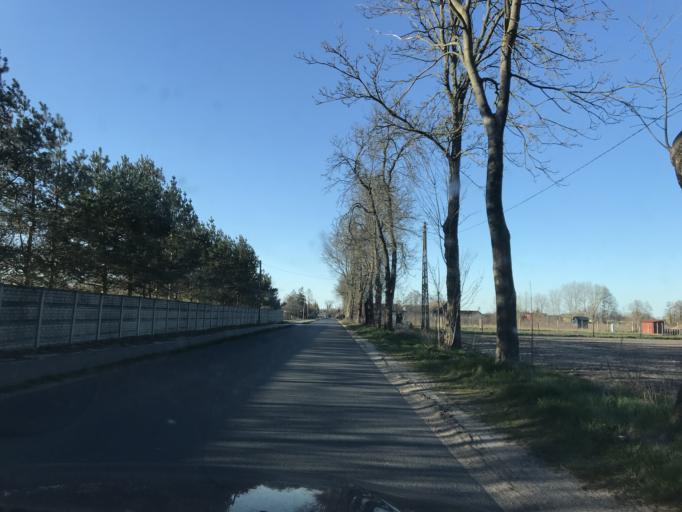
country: PL
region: Lubusz
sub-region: Powiat gorzowski
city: Deszczno
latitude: 52.6566
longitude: 15.3139
